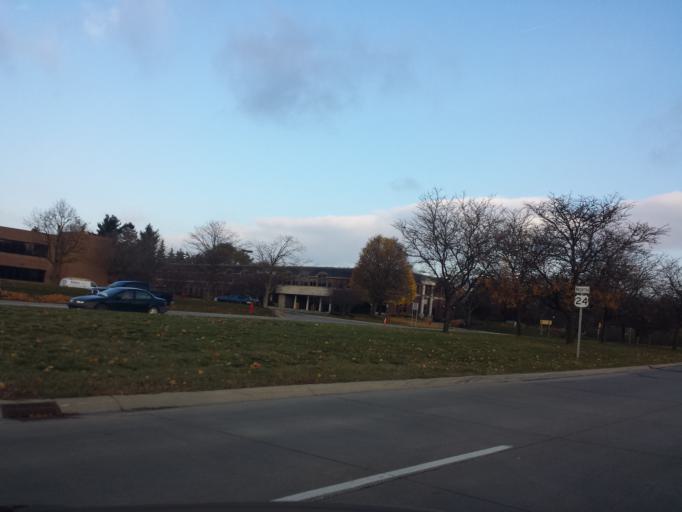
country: US
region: Michigan
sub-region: Oakland County
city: Bloomfield Hills
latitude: 42.5815
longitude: -83.2808
